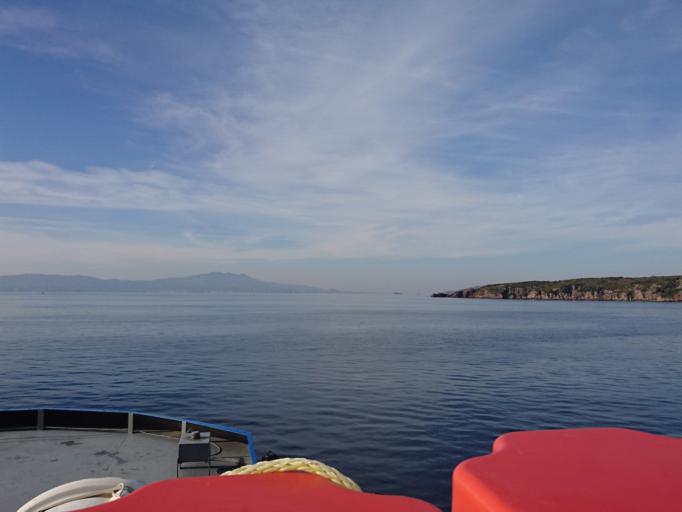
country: TR
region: Mugla
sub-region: Bodrum
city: Bodrum
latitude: 36.9955
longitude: 27.3976
